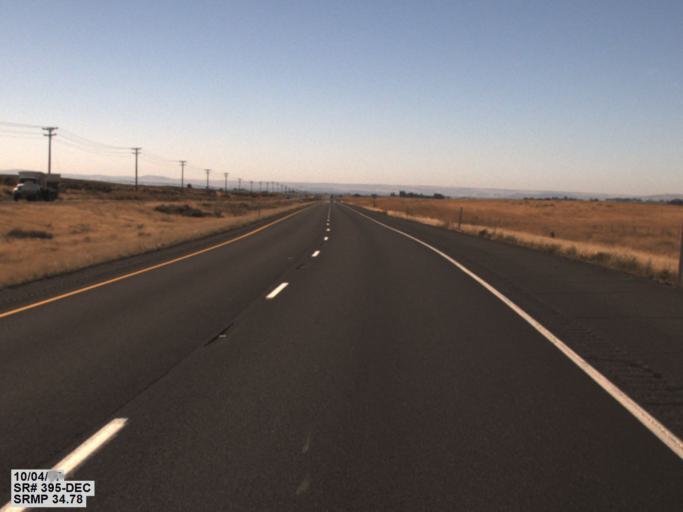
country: US
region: Washington
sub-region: Franklin County
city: Pasco
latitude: 46.4174
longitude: -119.0441
